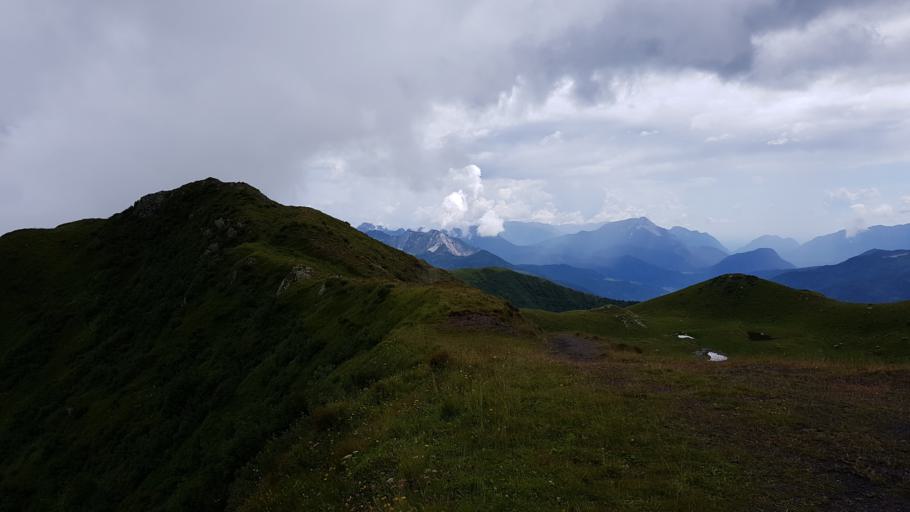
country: IT
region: Friuli Venezia Giulia
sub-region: Provincia di Udine
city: Cercivento
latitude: 46.5680
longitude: 12.9570
